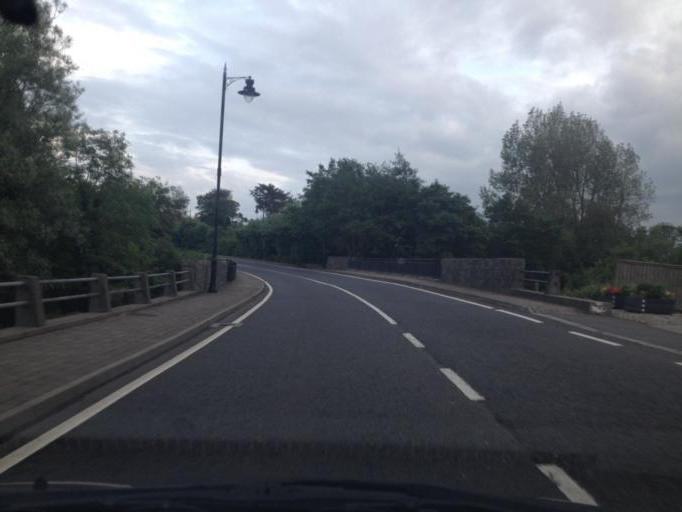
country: IE
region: Connaught
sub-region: Sligo
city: Sligo
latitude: 54.3287
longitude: -8.5010
